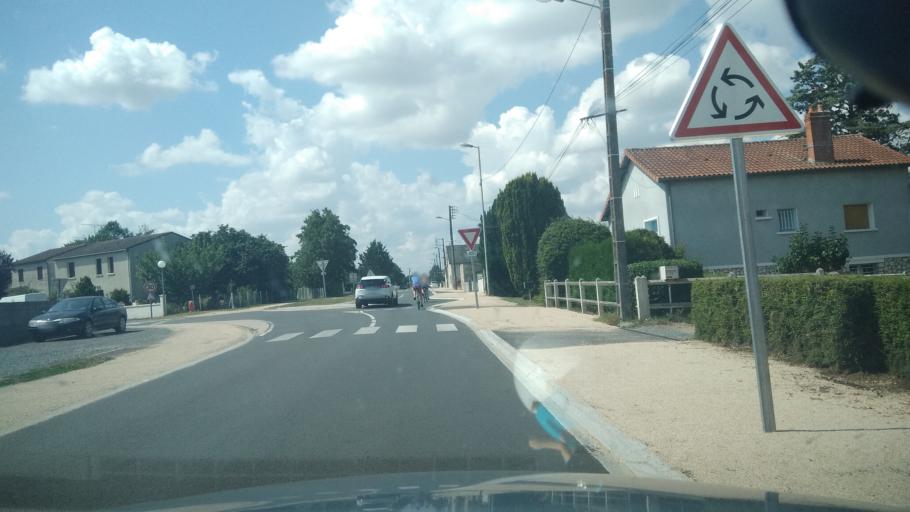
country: FR
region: Poitou-Charentes
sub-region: Departement de la Vienne
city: Dange-Saint-Romain
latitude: 46.9333
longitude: 0.5967
